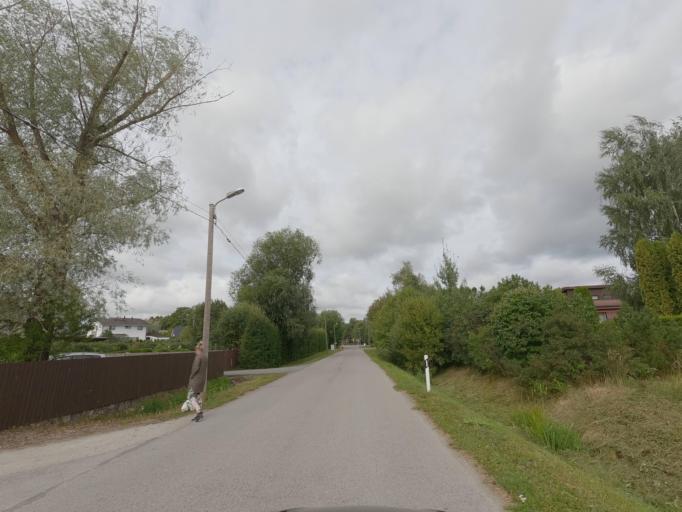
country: EE
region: Harju
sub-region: Saue vald
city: Laagri
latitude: 59.3498
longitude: 24.6405
